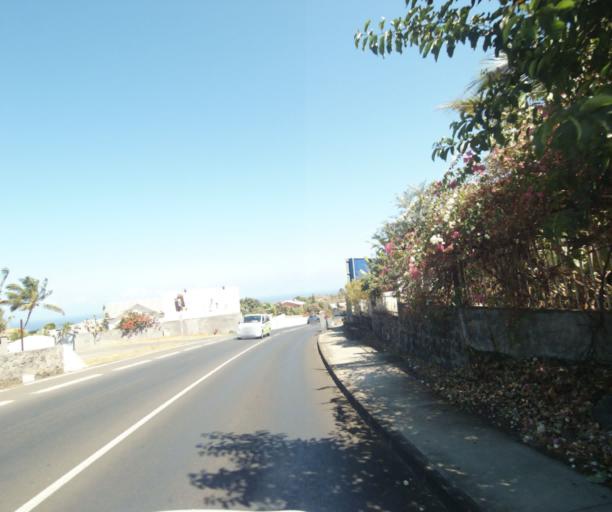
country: RE
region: Reunion
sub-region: Reunion
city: Le Port
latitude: -20.9779
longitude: 55.3212
